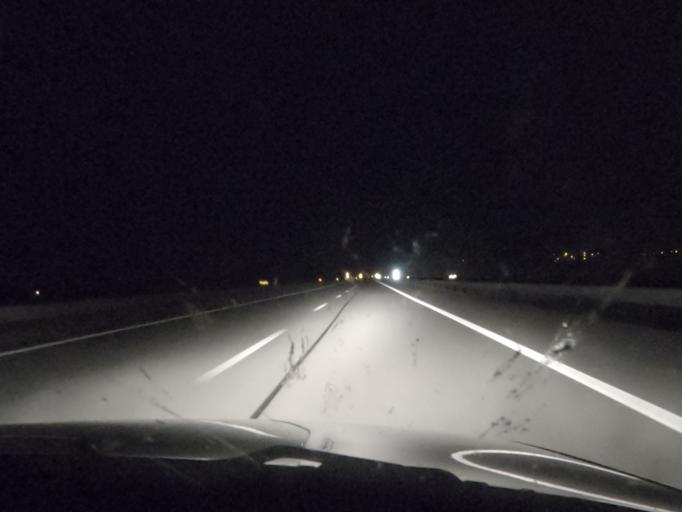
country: PT
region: Evora
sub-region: Estremoz
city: Estremoz
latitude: 38.8335
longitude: -7.6120
